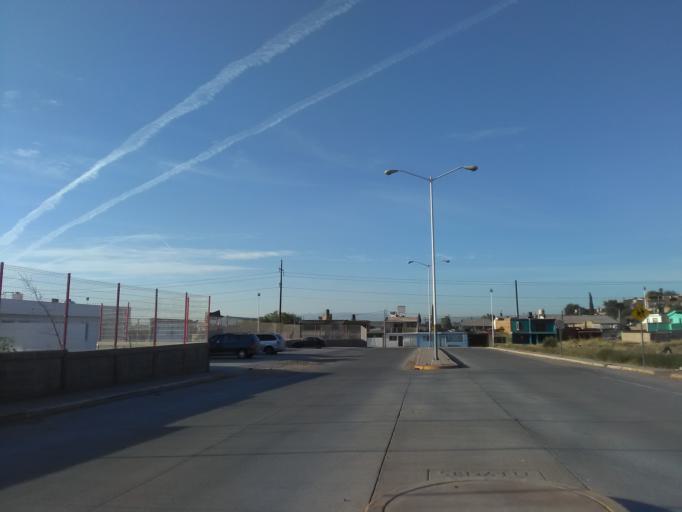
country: MX
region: Durango
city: Victoria de Durango
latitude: 24.0478
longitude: -104.6633
